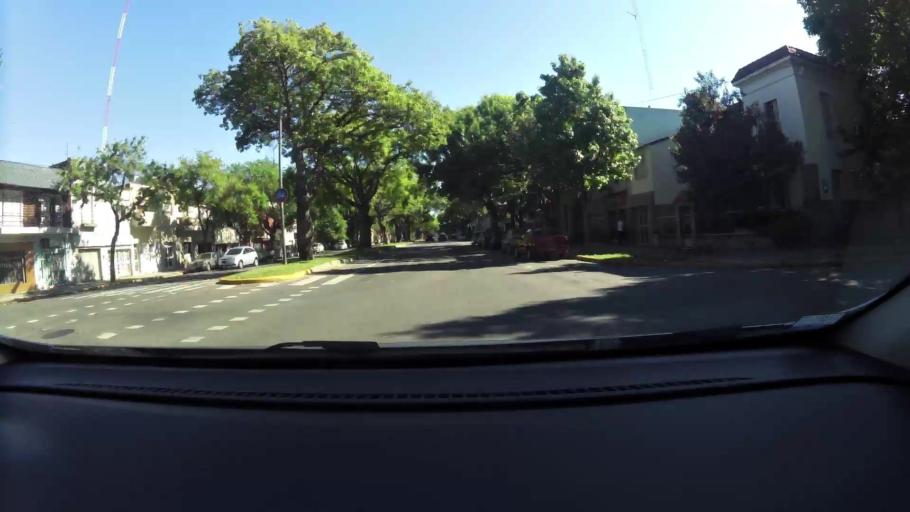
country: AR
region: Santa Fe
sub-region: Departamento de Rosario
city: Rosario
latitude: -32.9605
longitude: -60.6702
